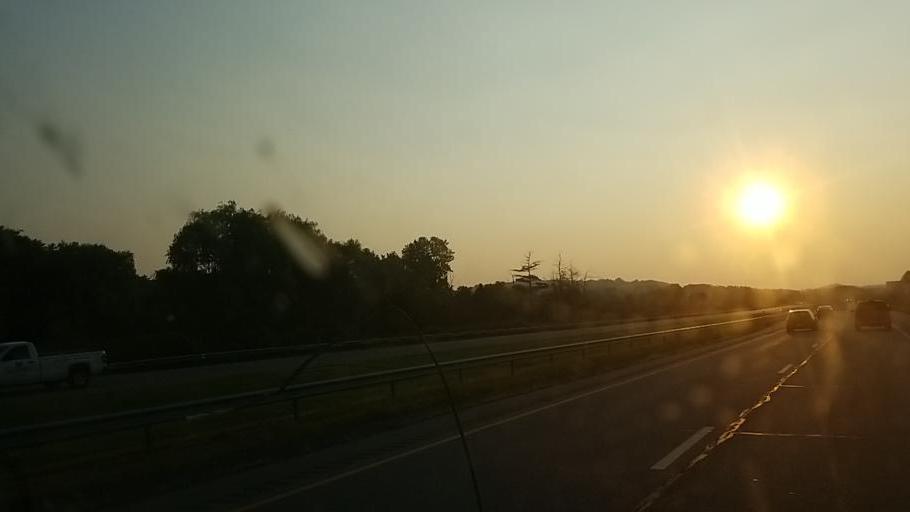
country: US
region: New York
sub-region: Montgomery County
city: Saint Johnsville
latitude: 43.0048
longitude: -74.7708
